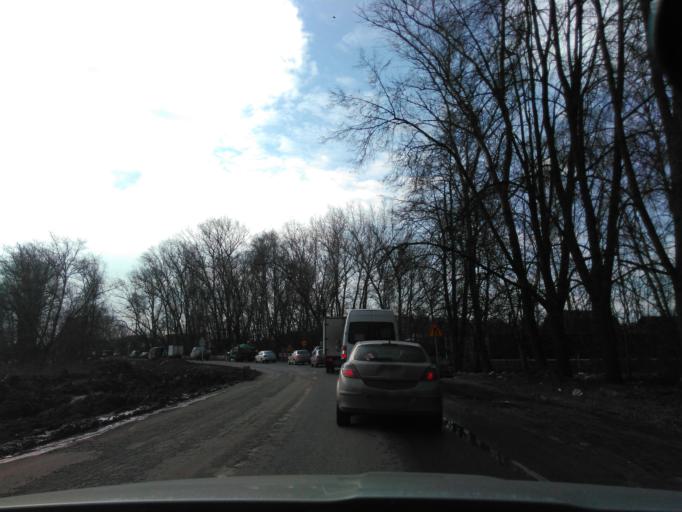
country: RU
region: Moscow
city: Severnyy
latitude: 55.9592
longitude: 37.5317
